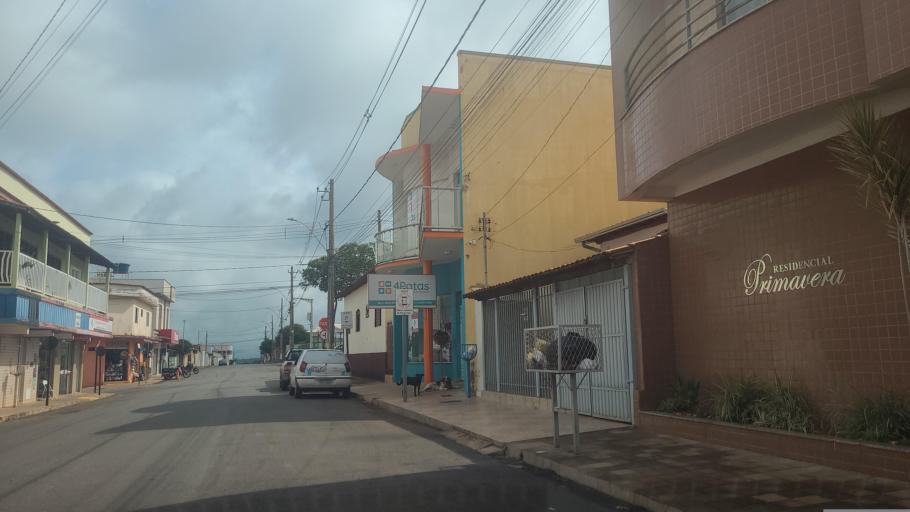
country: BR
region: Minas Gerais
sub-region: Carmo Do Paranaiba
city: Carmo do Paranaiba
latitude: -19.1949
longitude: -46.2425
